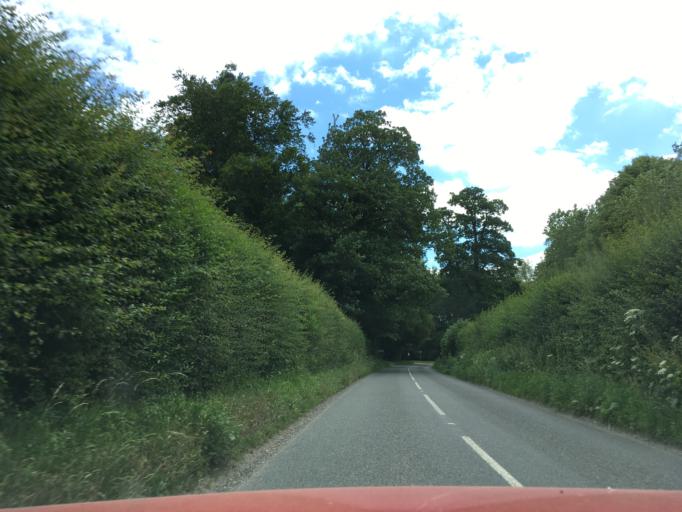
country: GB
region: England
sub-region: West Berkshire
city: Welford
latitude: 51.4587
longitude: -1.4134
